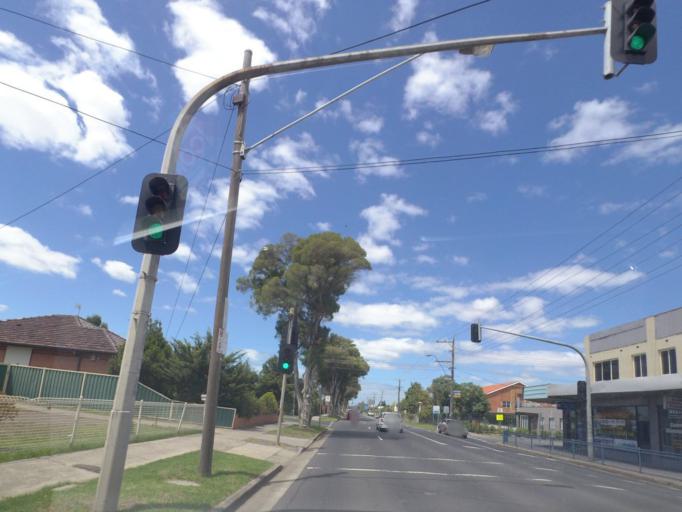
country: AU
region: Victoria
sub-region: Brimbank
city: Sunshine North
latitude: -37.7693
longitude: 144.8302
